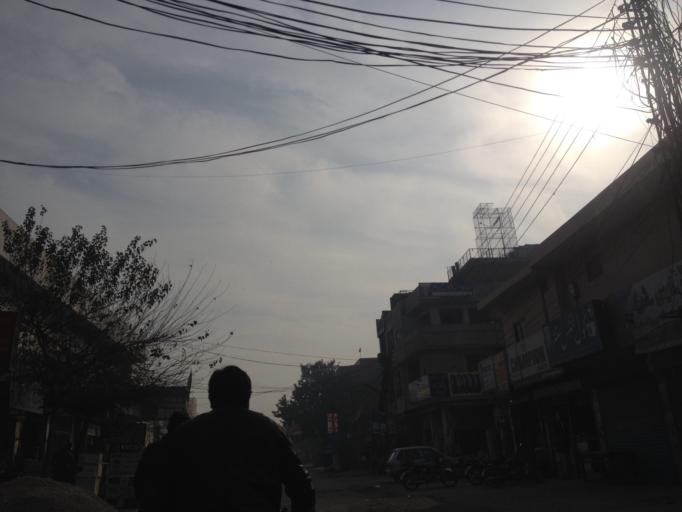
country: PK
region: Punjab
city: Lahore
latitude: 31.4662
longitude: 74.3066
